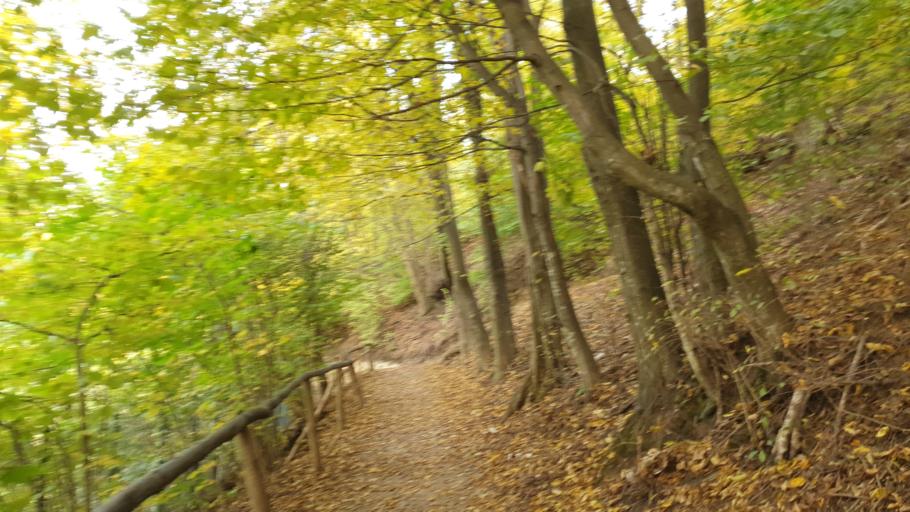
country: PL
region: Lublin Voivodeship
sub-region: Powiat pulawski
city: Kazimierz Dolny
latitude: 51.3227
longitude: 21.9511
